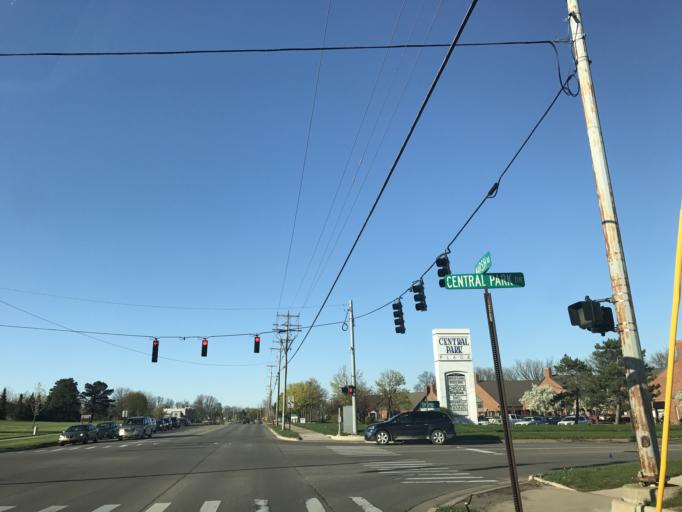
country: US
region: Michigan
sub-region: Ingham County
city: Okemos
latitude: 42.7271
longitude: -84.4145
